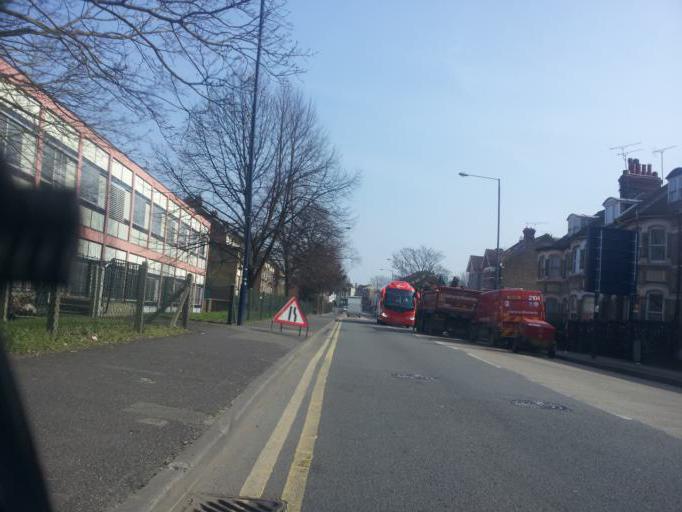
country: GB
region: England
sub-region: Kent
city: Gravesend
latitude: 51.4410
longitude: 0.3758
